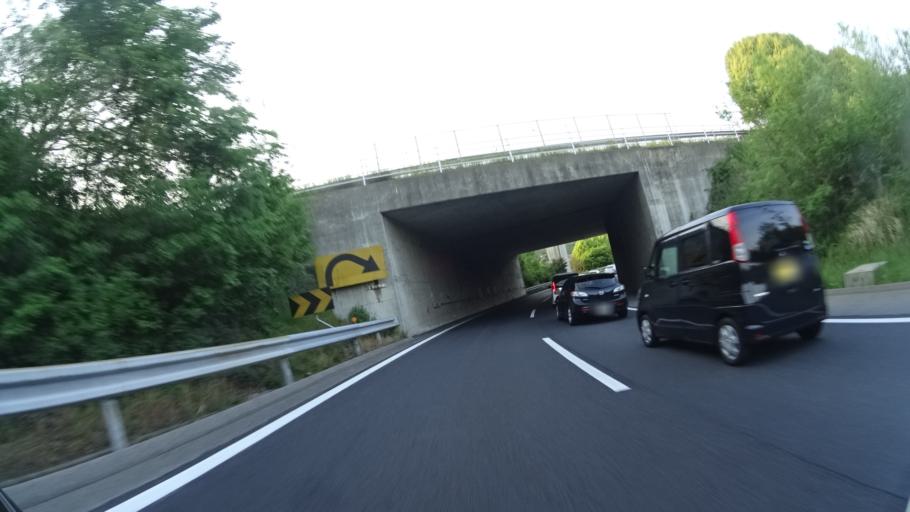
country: JP
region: Okayama
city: Kurashiki
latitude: 34.6265
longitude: 133.7931
